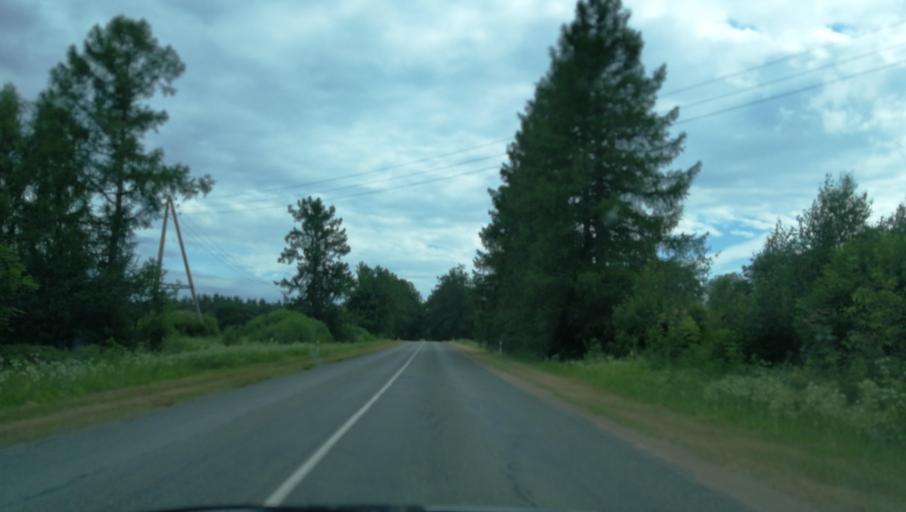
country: LV
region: Valmieras Rajons
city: Valmiera
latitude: 57.6851
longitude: 25.4300
